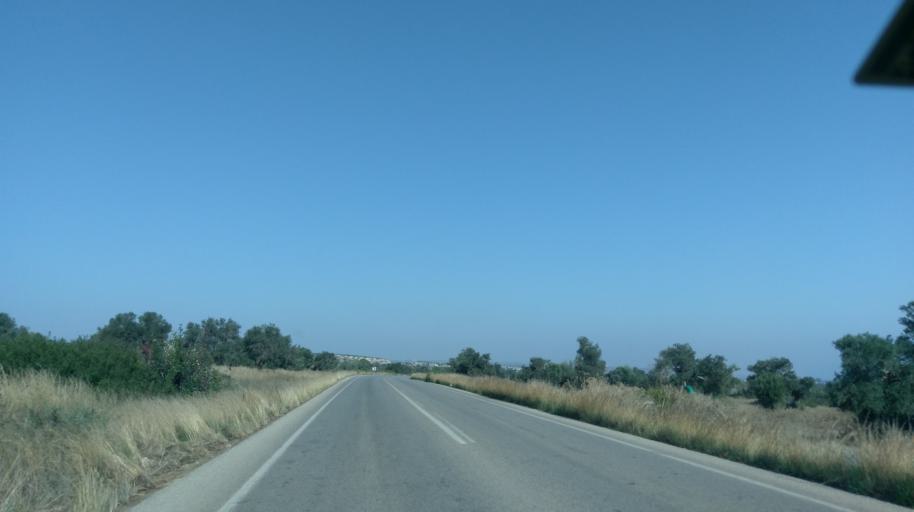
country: CY
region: Ammochostos
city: Leonarisso
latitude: 35.4076
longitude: 34.1093
